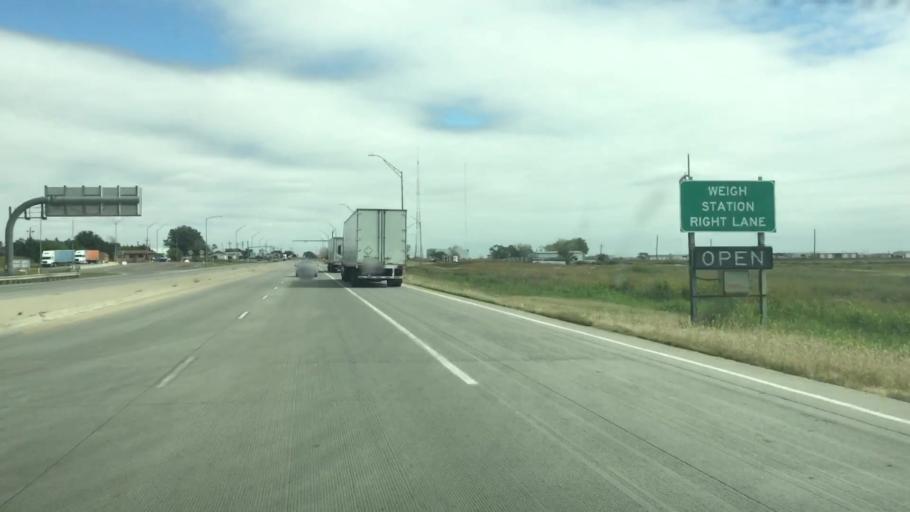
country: US
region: Colorado
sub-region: Prowers County
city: Lamar
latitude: 38.1140
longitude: -102.6313
